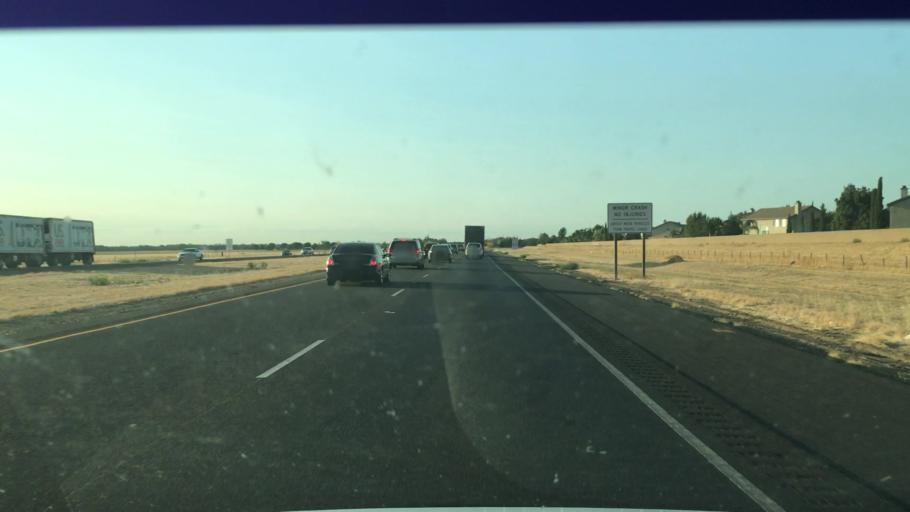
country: US
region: California
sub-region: Sacramento County
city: Laguna
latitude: 38.3977
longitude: -121.4813
